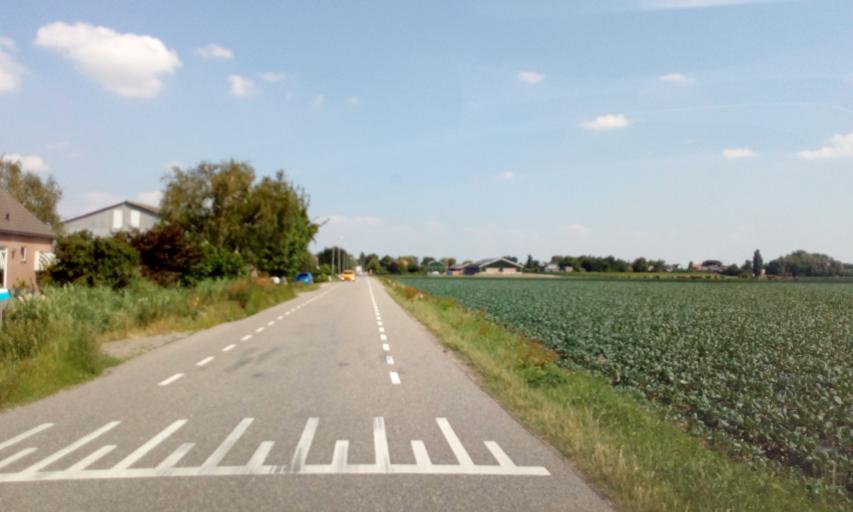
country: NL
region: South Holland
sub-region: Gemeente Rijnwoude
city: Benthuizen
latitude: 52.0899
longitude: 4.5564
